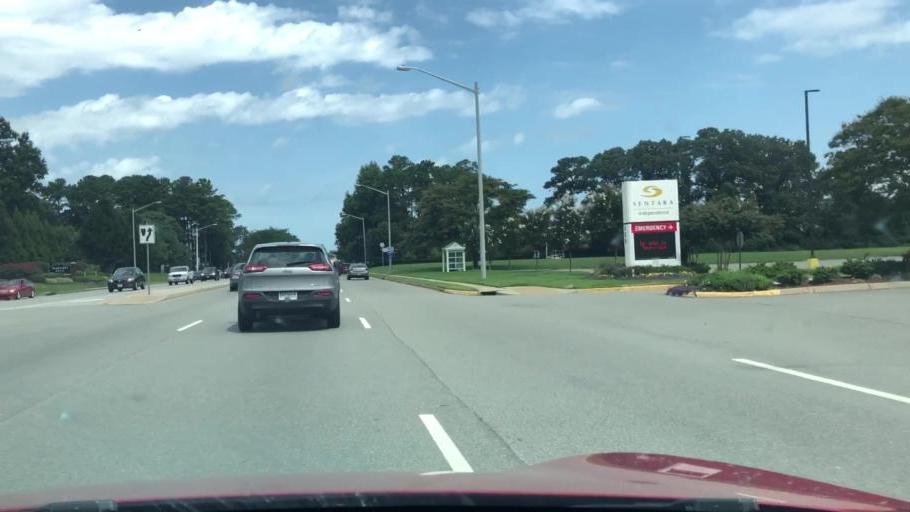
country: US
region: Virginia
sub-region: City of Chesapeake
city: Chesapeake
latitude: 36.8677
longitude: -76.1327
